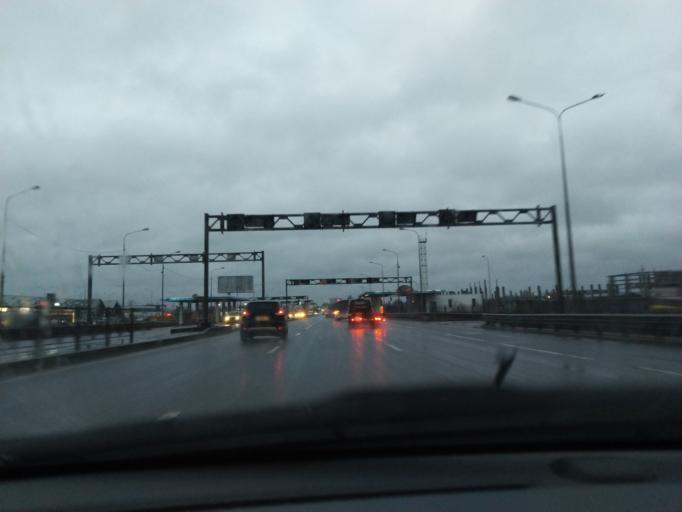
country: RU
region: St.-Petersburg
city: Uritsk
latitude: 59.8083
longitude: 30.1668
